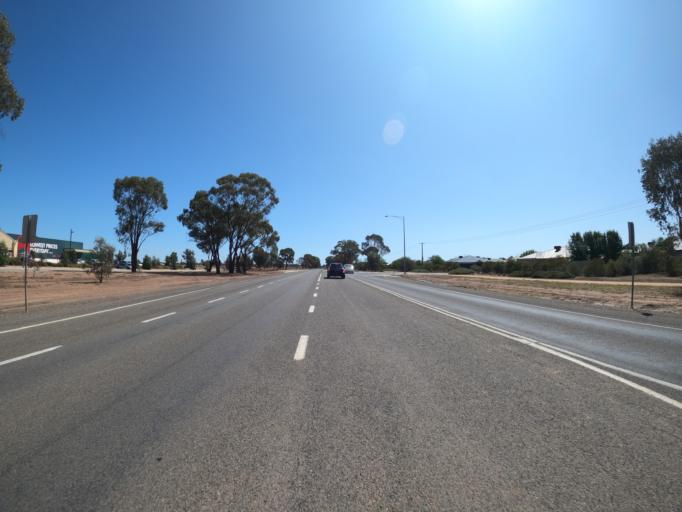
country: AU
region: Victoria
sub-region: Moira
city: Yarrawonga
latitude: -36.0111
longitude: 146.0261
